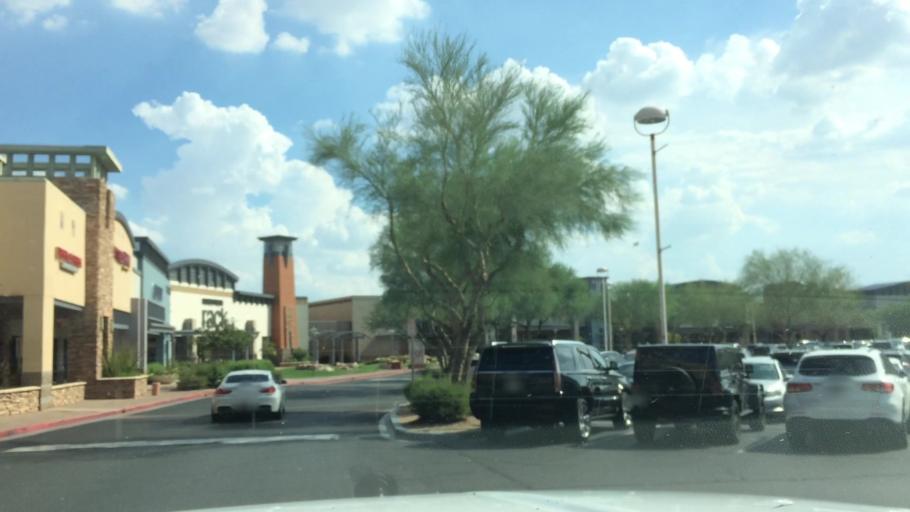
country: US
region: Arizona
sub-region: Maricopa County
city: Paradise Valley
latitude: 33.6349
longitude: -111.9214
